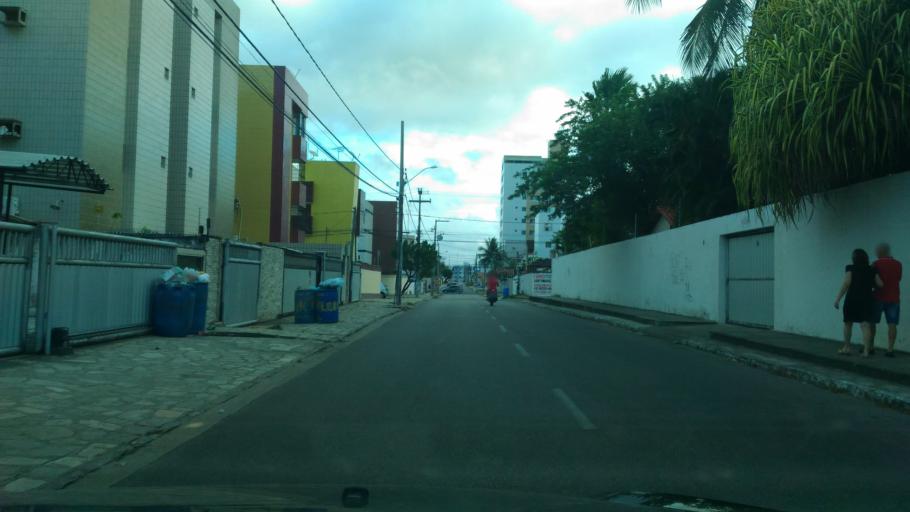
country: BR
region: Paraiba
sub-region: Joao Pessoa
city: Joao Pessoa
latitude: -7.1549
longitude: -34.8373
